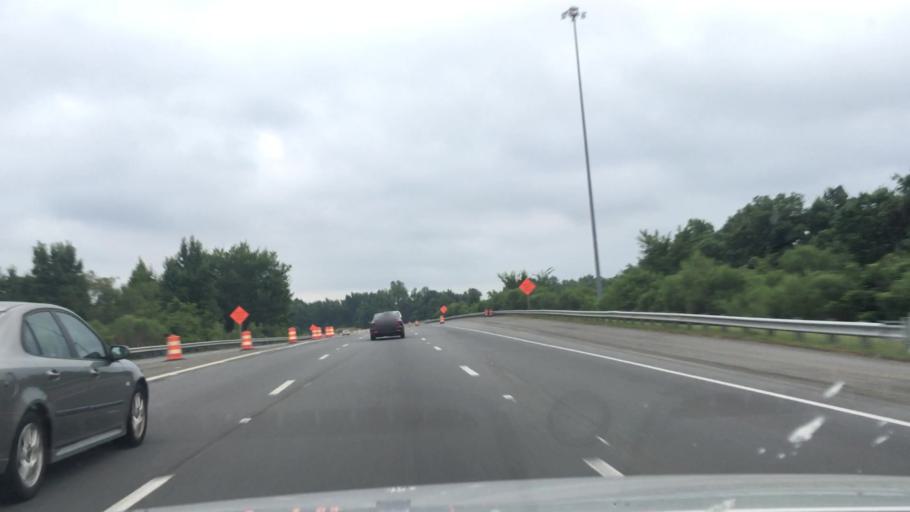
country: US
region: North Carolina
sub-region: Mecklenburg County
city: Charlotte
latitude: 35.2744
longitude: -80.8463
